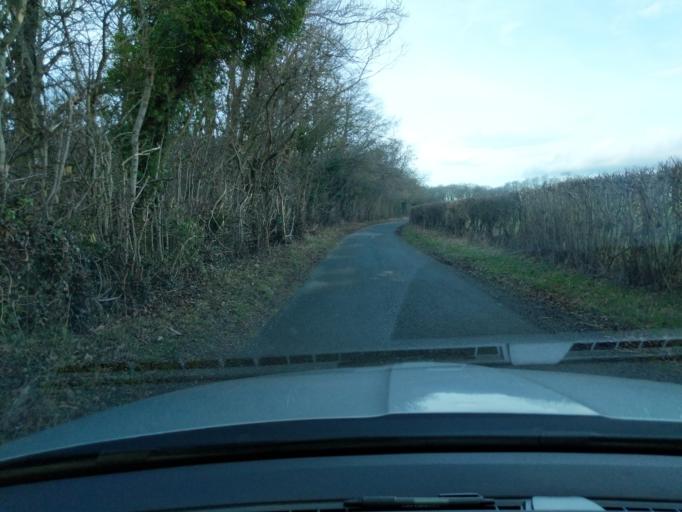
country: GB
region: England
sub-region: North Yorkshire
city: Catterick
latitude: 54.3705
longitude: -1.6717
